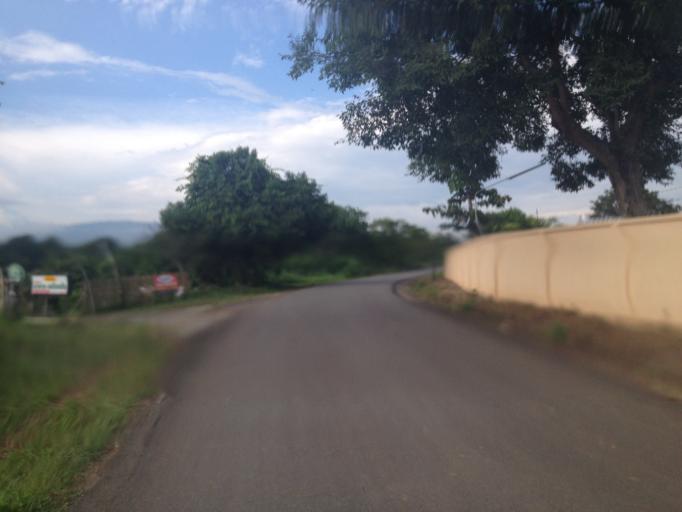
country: TH
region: Chiang Mai
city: Hang Dong
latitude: 18.7137
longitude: 98.9043
